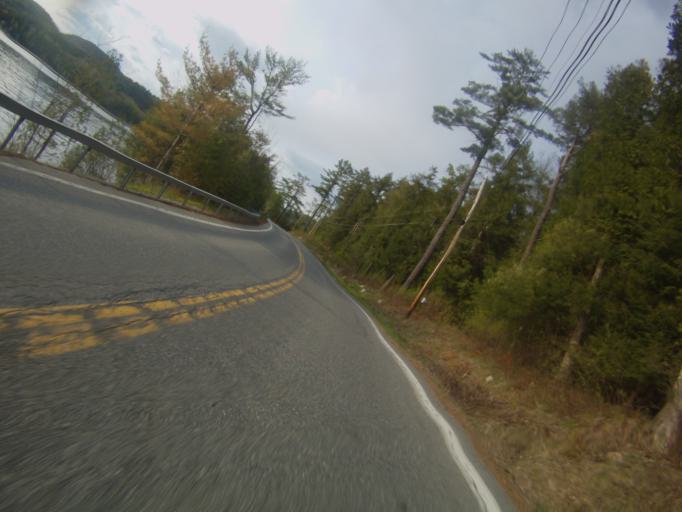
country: US
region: New York
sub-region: Warren County
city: Warrensburg
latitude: 43.7016
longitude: -73.7125
